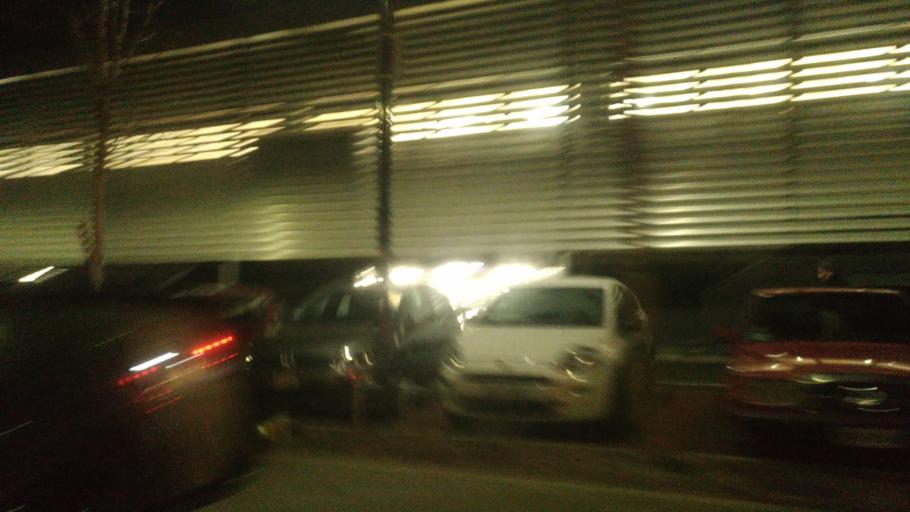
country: IT
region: Emilia-Romagna
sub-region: Provincia di Bologna
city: Progresso
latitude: 44.5314
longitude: 11.3525
